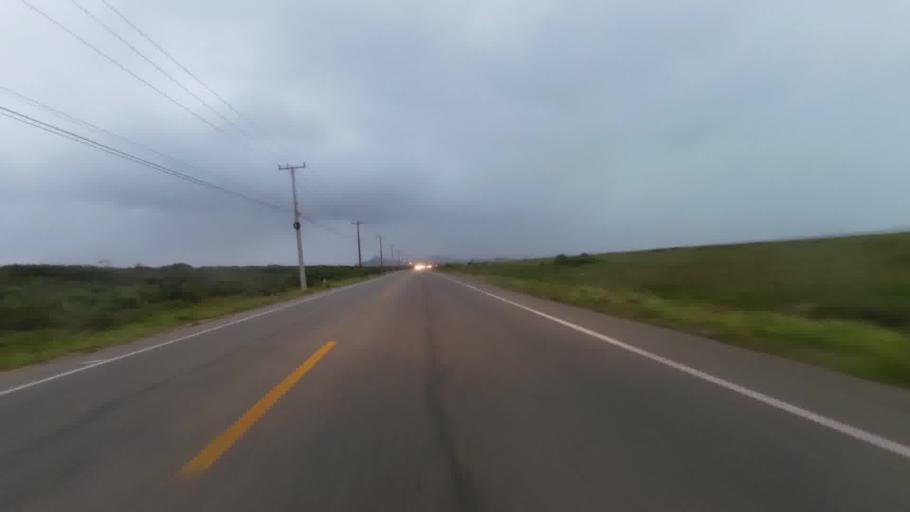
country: BR
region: Espirito Santo
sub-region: Itapemirim
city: Itapemirim
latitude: -20.9734
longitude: -40.8114
